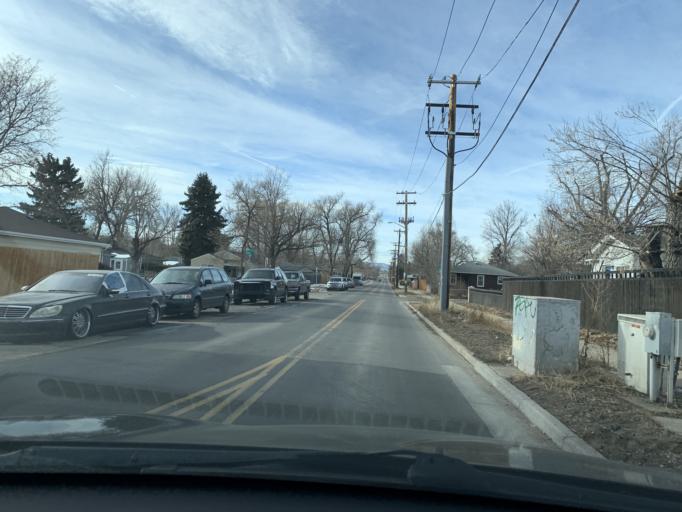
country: US
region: Colorado
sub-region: Denver County
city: Denver
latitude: 39.7330
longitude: -105.0258
